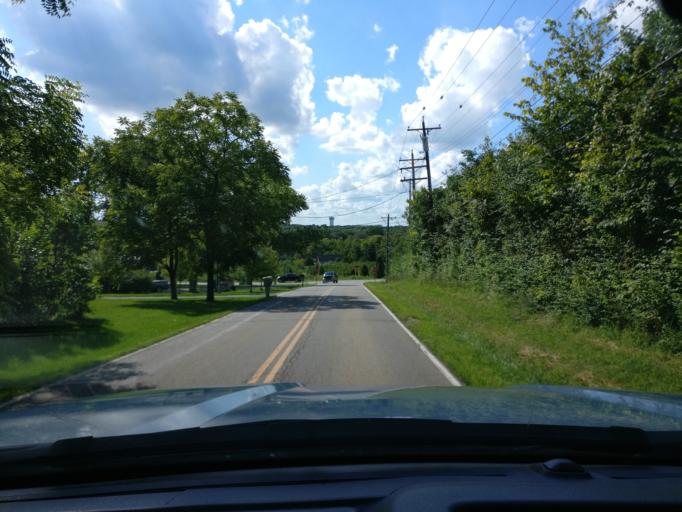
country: US
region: Ohio
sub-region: Warren County
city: Springboro
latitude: 39.5076
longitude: -84.2384
